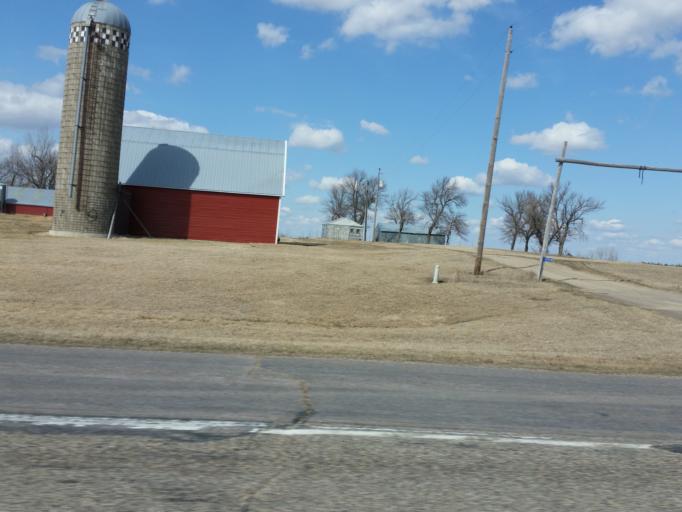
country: US
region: South Dakota
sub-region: Deuel County
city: Clear Lake
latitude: 44.8901
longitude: -96.6937
